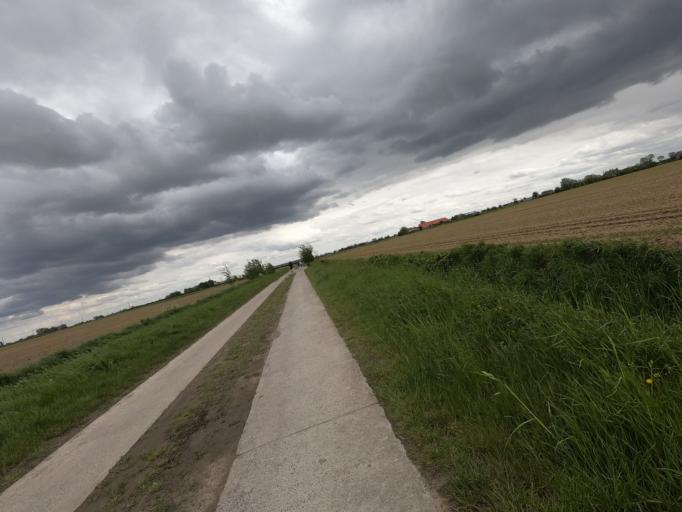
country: BE
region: Flanders
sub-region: Provincie West-Vlaanderen
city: Alveringem
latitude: 50.9376
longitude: 2.7513
